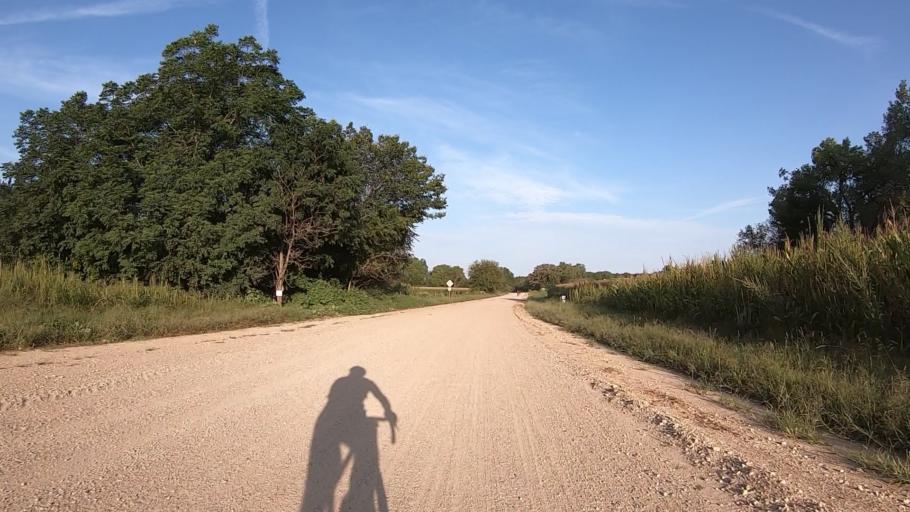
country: US
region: Kansas
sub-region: Marshall County
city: Blue Rapids
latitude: 39.7204
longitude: -96.7693
